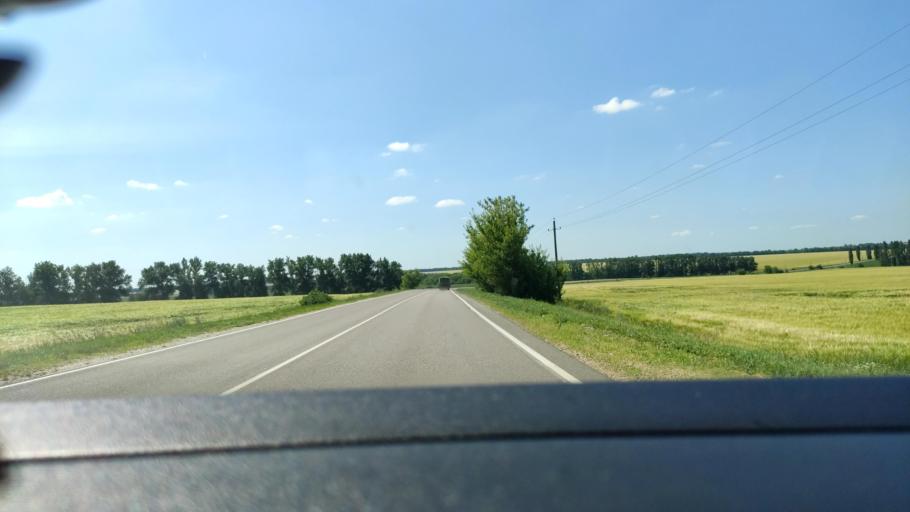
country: RU
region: Voronezj
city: Novaya Usman'
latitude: 51.5588
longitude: 39.3762
